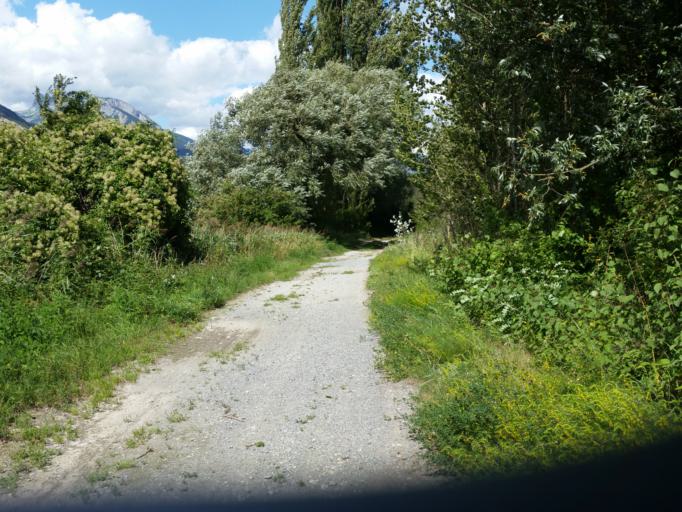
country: CH
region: Valais
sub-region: Martigny District
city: Riddes
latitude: 46.1801
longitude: 7.2332
